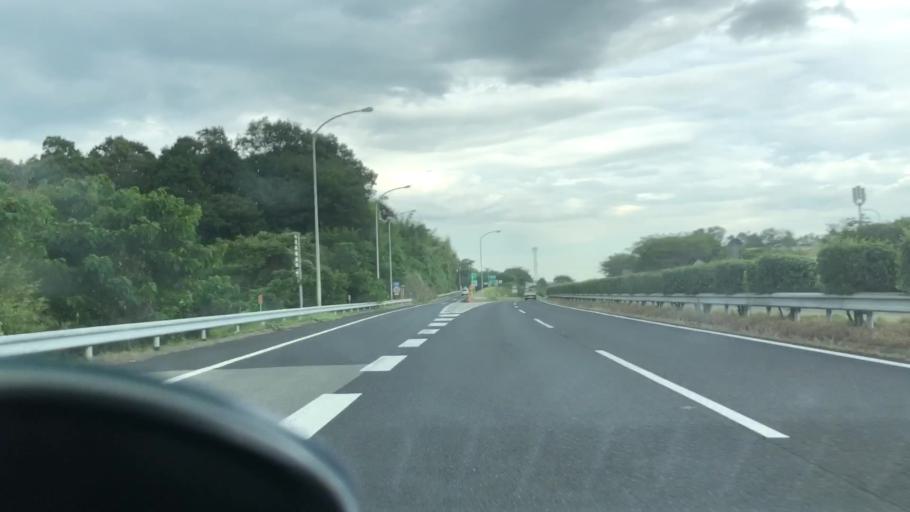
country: JP
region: Hyogo
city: Himeji
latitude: 34.9480
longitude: 134.7973
